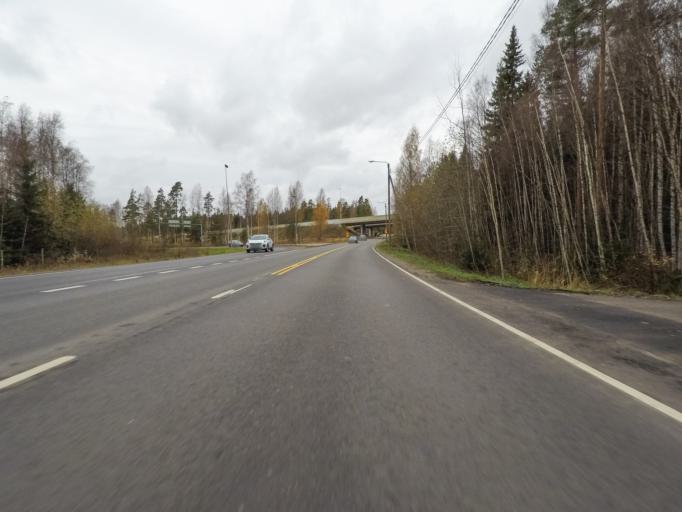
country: FI
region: Uusimaa
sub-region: Porvoo
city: Porvoo
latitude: 60.4154
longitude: 25.6733
